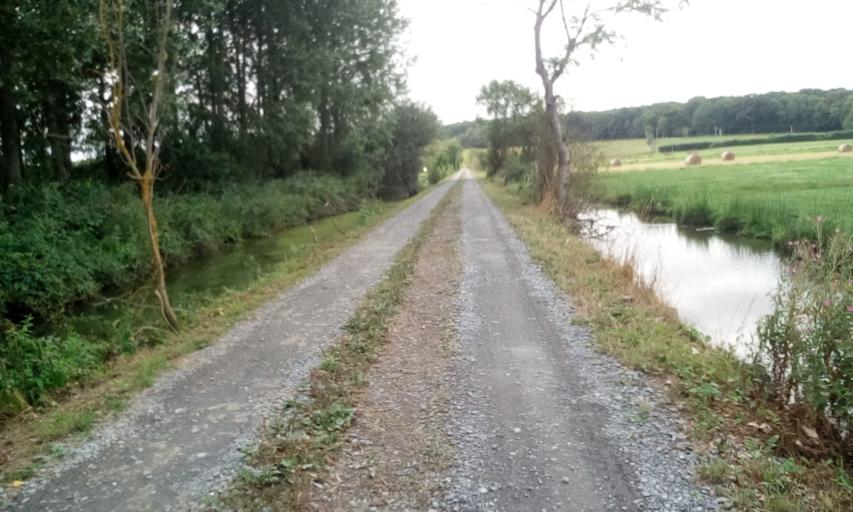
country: FR
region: Lower Normandy
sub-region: Departement du Calvados
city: Bavent
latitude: 49.2145
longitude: -0.1740
